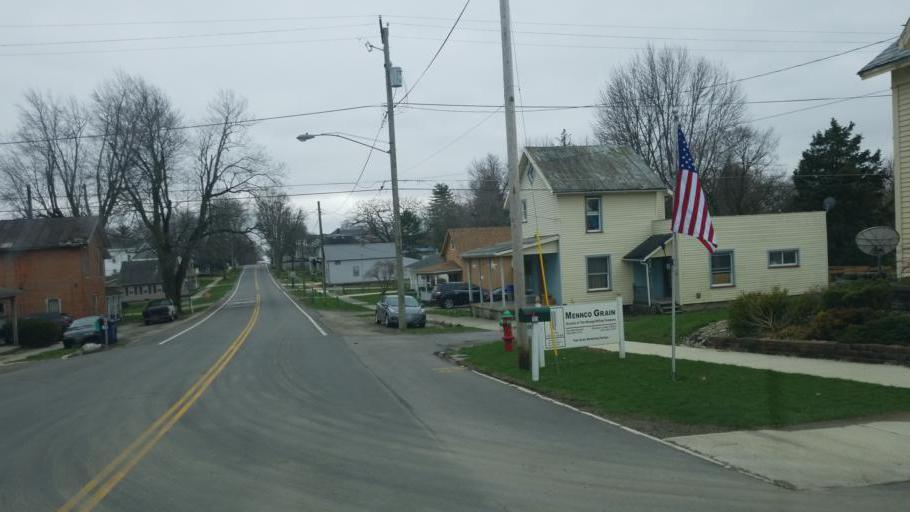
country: US
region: Ohio
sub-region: Wyandot County
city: Upper Sandusky
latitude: 40.8173
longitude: -83.1309
